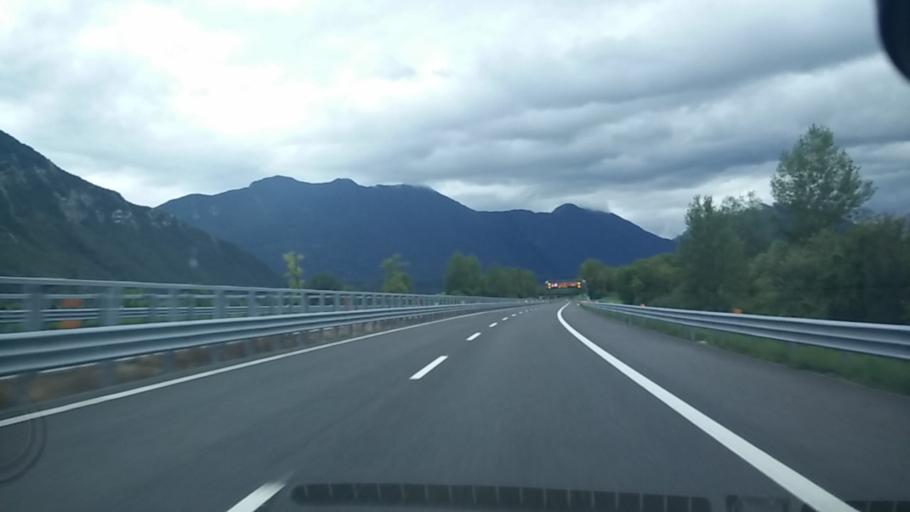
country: IT
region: Friuli Venezia Giulia
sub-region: Provincia di Udine
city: Amaro
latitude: 46.3719
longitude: 13.0999
